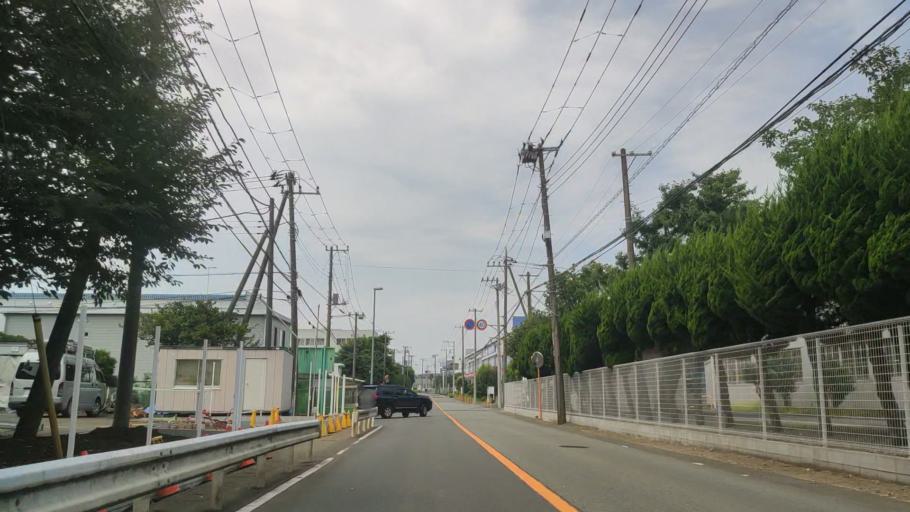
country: JP
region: Kanagawa
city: Fujisawa
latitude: 35.4027
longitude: 139.4261
